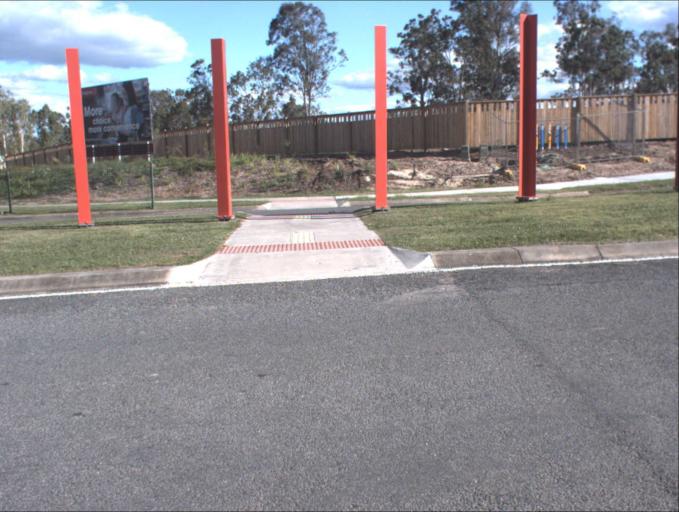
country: AU
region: Queensland
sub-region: Logan
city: North Maclean
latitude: -27.8091
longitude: 152.9555
